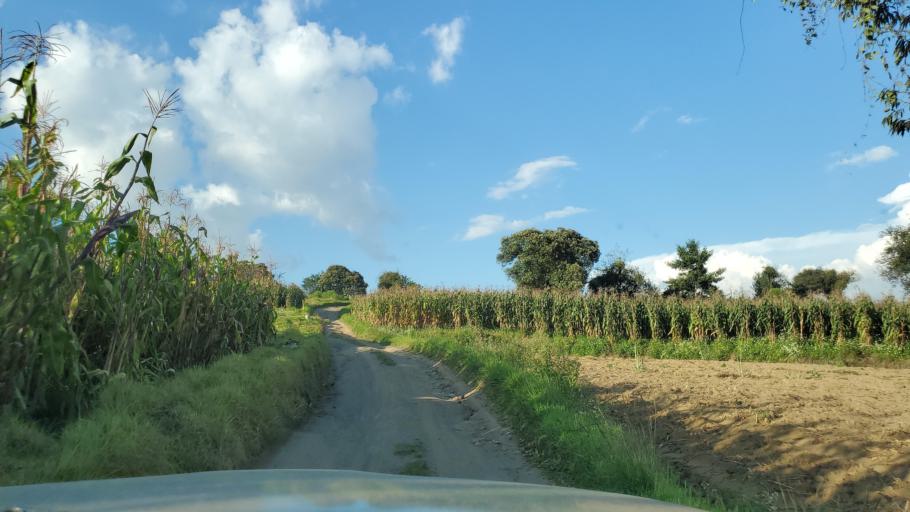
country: GT
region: Quetzaltenango
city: Quetzaltenango
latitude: 14.8368
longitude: -91.5507
